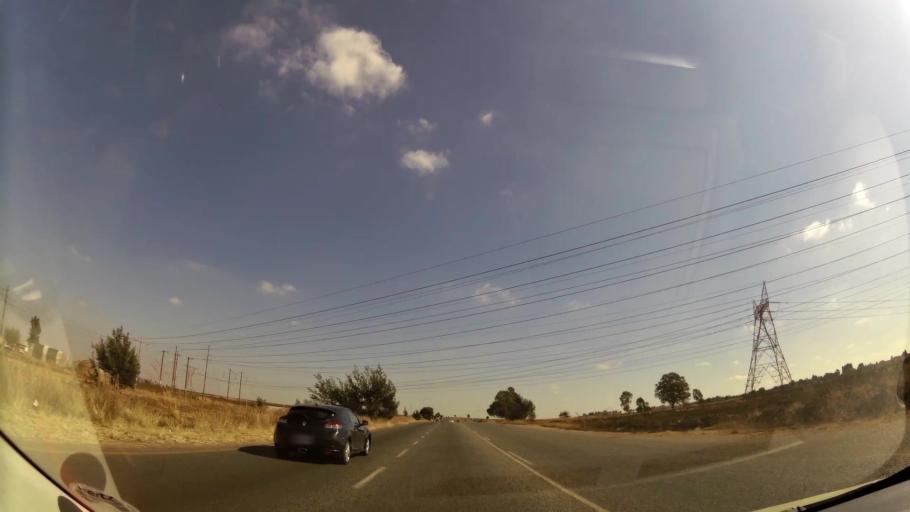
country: ZA
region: Gauteng
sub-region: West Rand District Municipality
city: Randfontein
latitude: -26.1811
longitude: 27.7534
